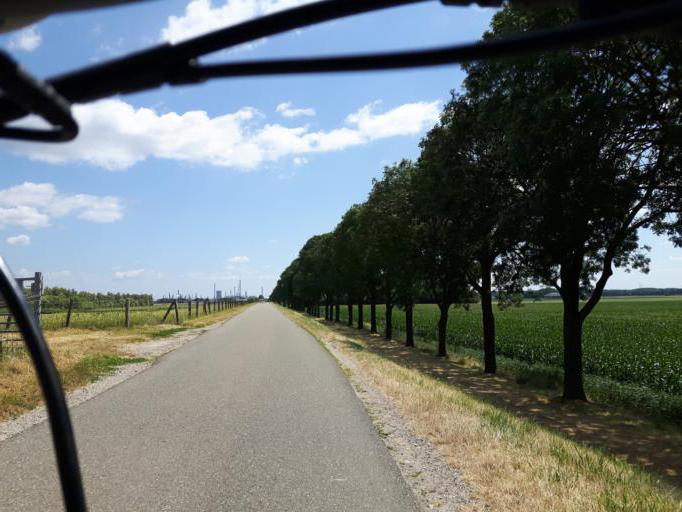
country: NL
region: North Brabant
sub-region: Gemeente Moerdijk
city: Klundert
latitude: 51.6792
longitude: 4.5060
